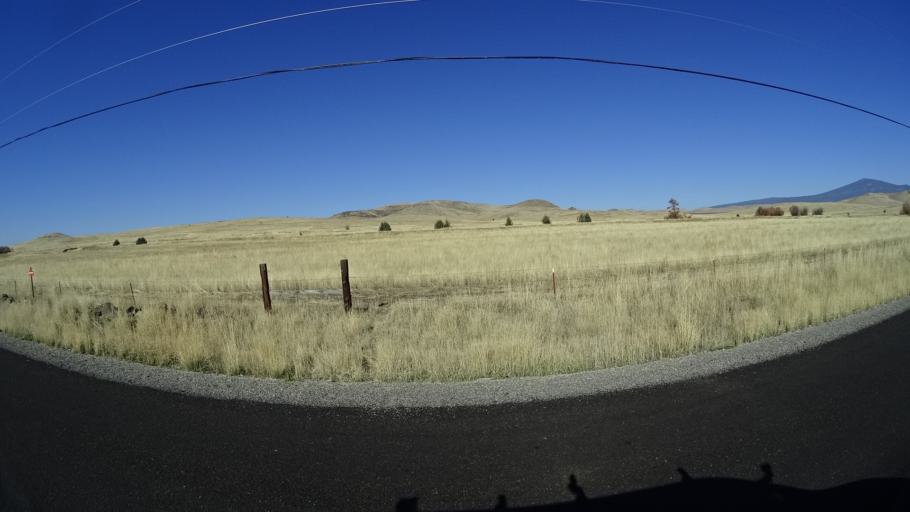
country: US
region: California
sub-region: Siskiyou County
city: Montague
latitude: 41.7262
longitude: -122.4203
